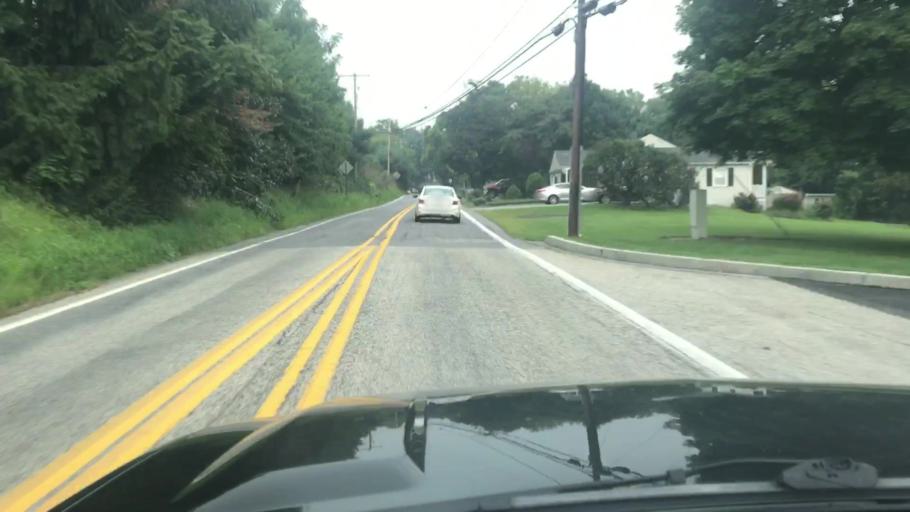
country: US
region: Pennsylvania
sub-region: Cumberland County
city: Shiremanstown
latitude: 40.2678
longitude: -76.9815
